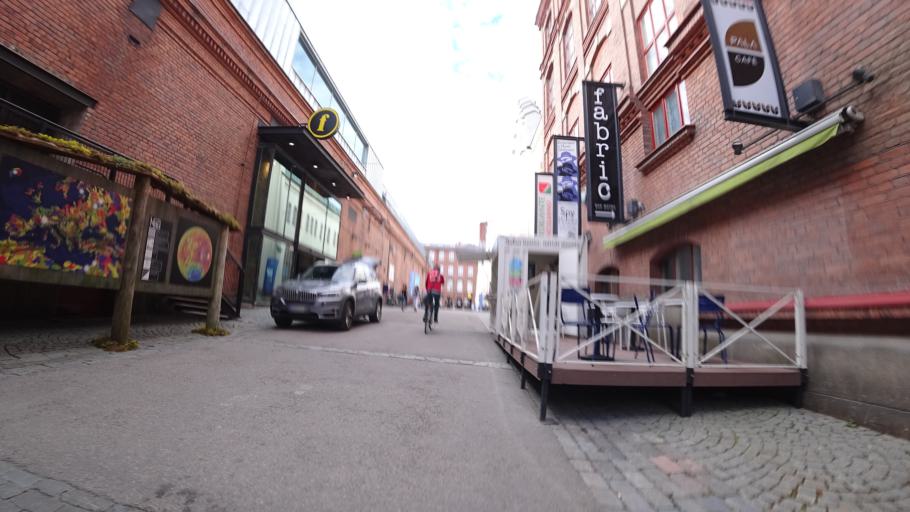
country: FI
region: Pirkanmaa
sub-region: Tampere
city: Tampere
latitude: 61.5011
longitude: 23.7588
